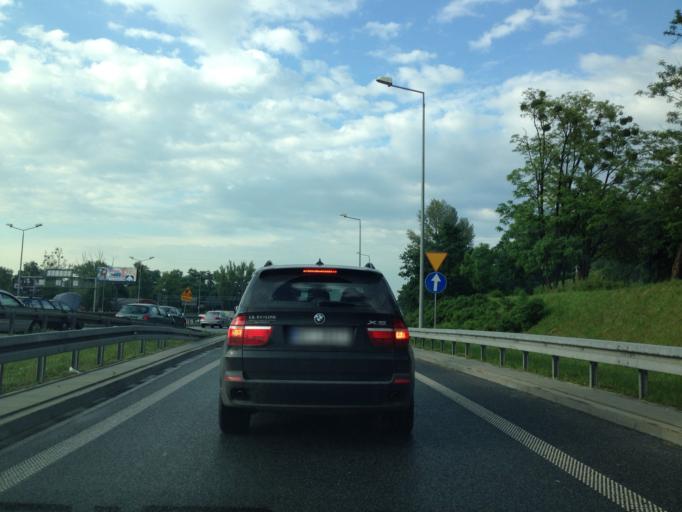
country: PL
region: Masovian Voivodeship
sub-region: Warszawa
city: Bielany
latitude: 52.2576
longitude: 20.9494
